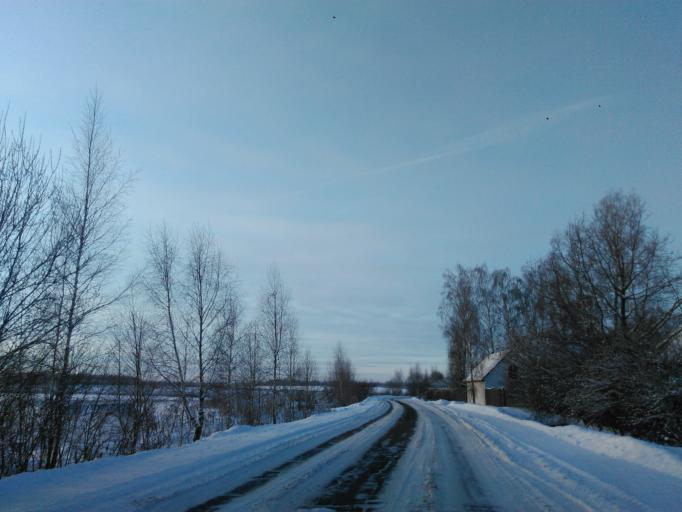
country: RU
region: Tverskaya
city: Zavidovo
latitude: 56.6383
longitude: 36.6298
